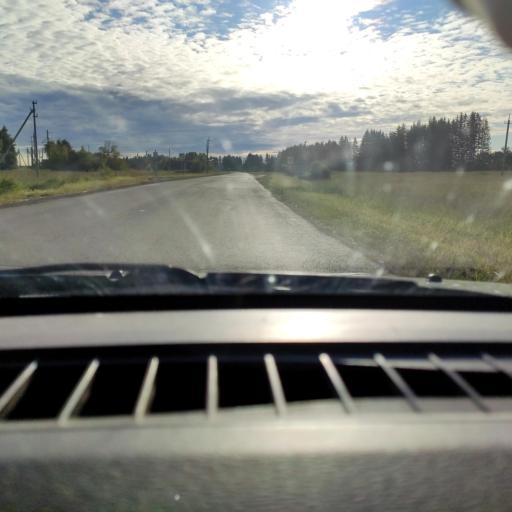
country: RU
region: Perm
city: Uinskoye
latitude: 57.0988
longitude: 56.6464
